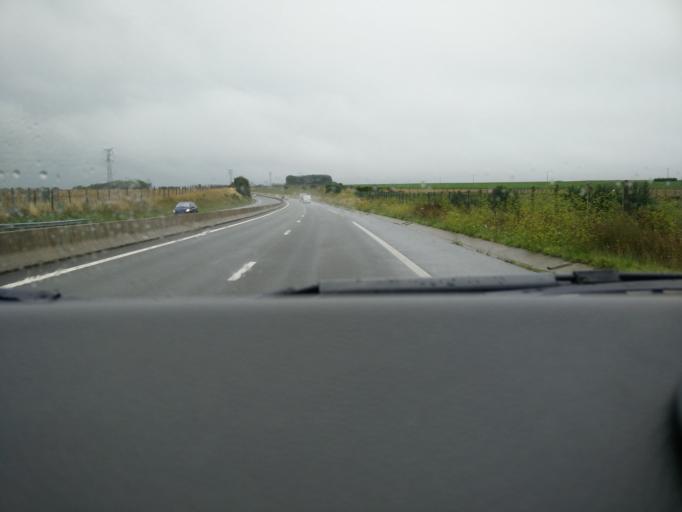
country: FR
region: Nord-Pas-de-Calais
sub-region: Departement du Pas-de-Calais
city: Marconnelle
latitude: 50.3626
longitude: 1.9728
